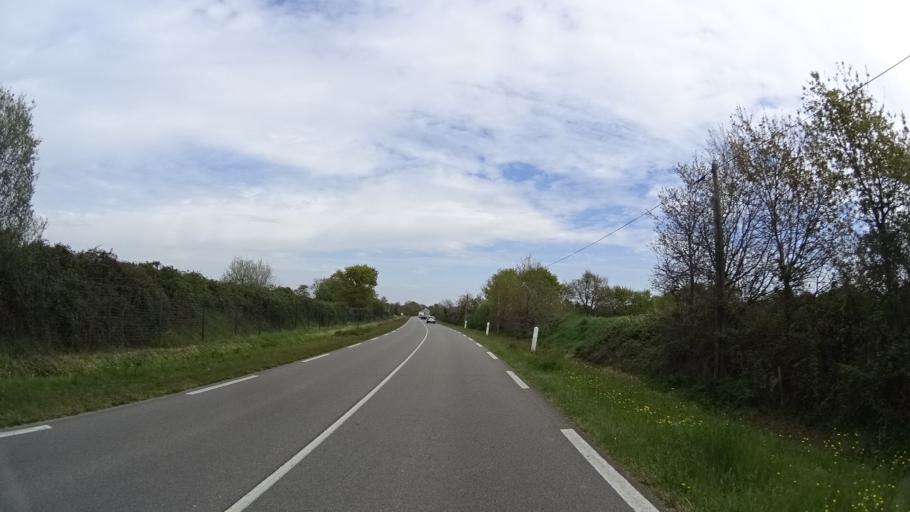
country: FR
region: Pays de la Loire
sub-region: Departement de la Loire-Atlantique
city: Bourgneuf-en-Retz
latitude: 47.0660
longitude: -1.9096
